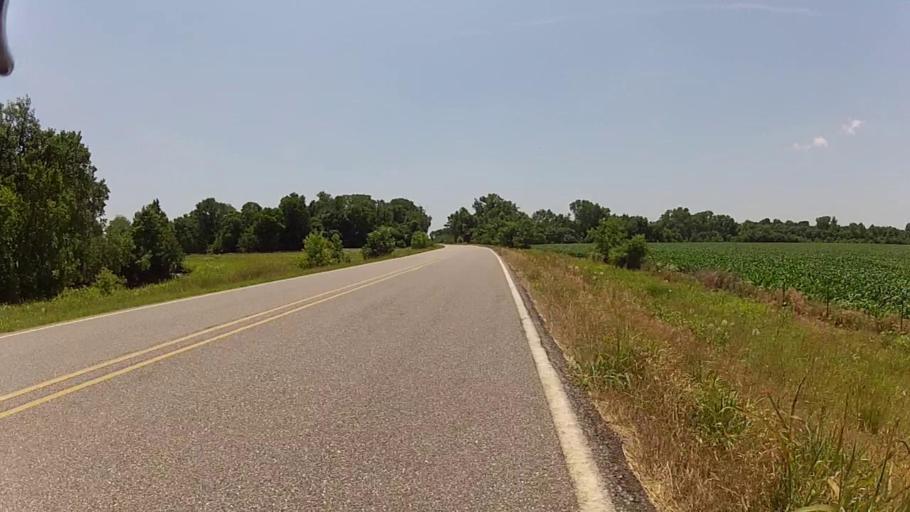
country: US
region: Kansas
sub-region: Montgomery County
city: Cherryvale
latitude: 37.2119
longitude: -95.5391
